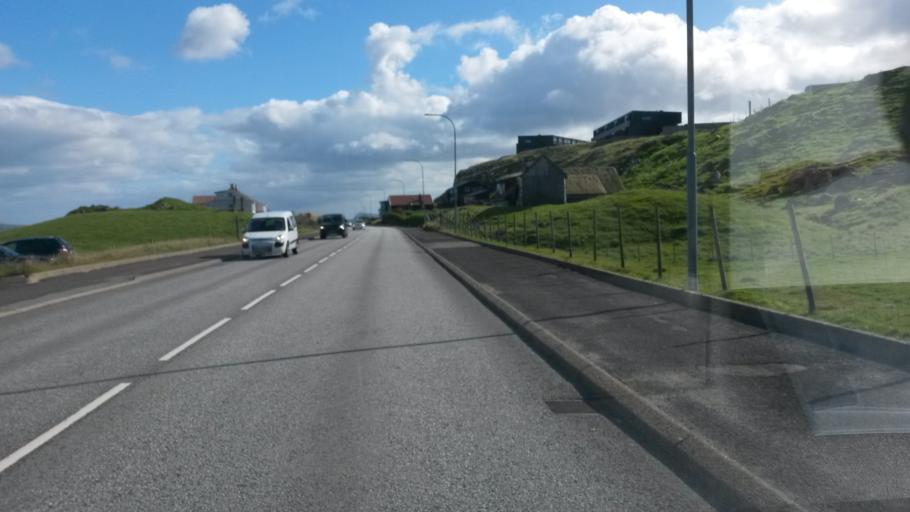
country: FO
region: Streymoy
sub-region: Torshavn
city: Torshavn
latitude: 62.0217
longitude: -6.7586
